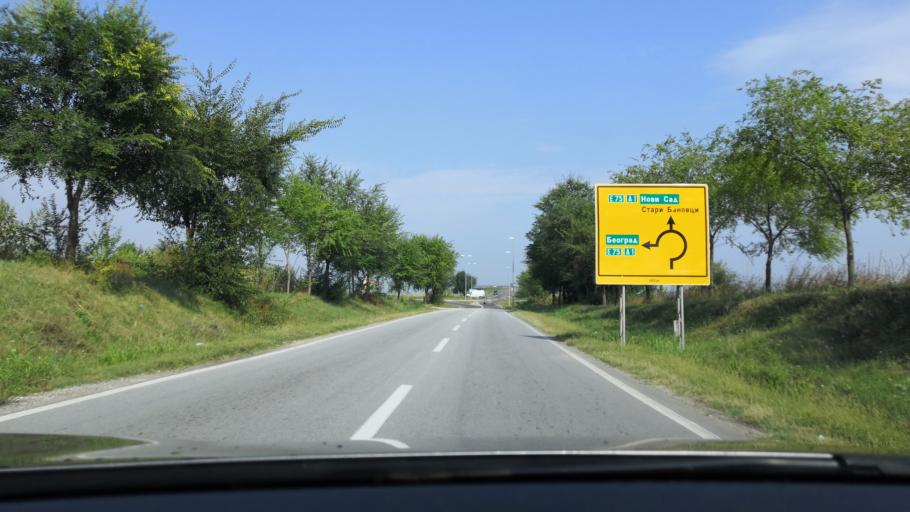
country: RS
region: Autonomna Pokrajina Vojvodina
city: Nova Pazova
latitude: 44.9663
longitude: 20.2325
